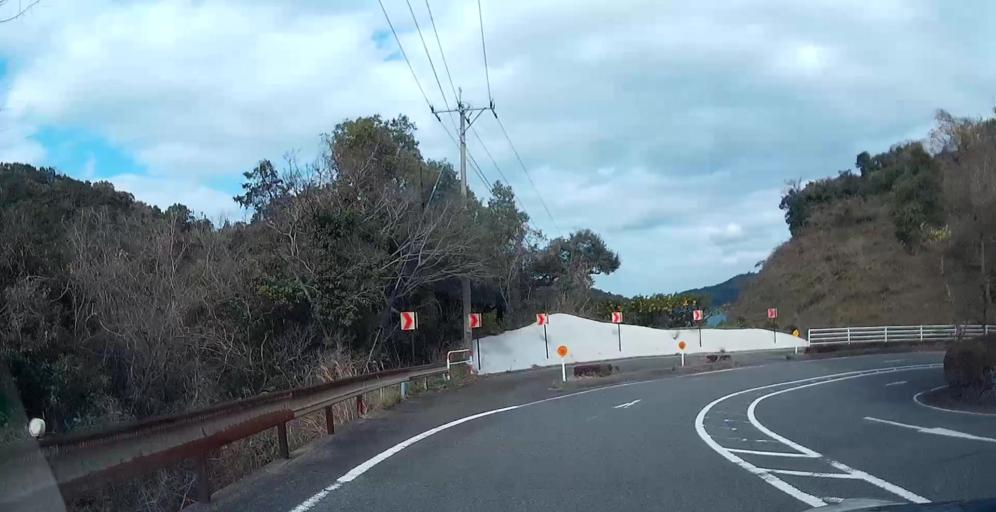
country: JP
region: Kumamoto
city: Minamata
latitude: 32.3258
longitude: 130.4742
